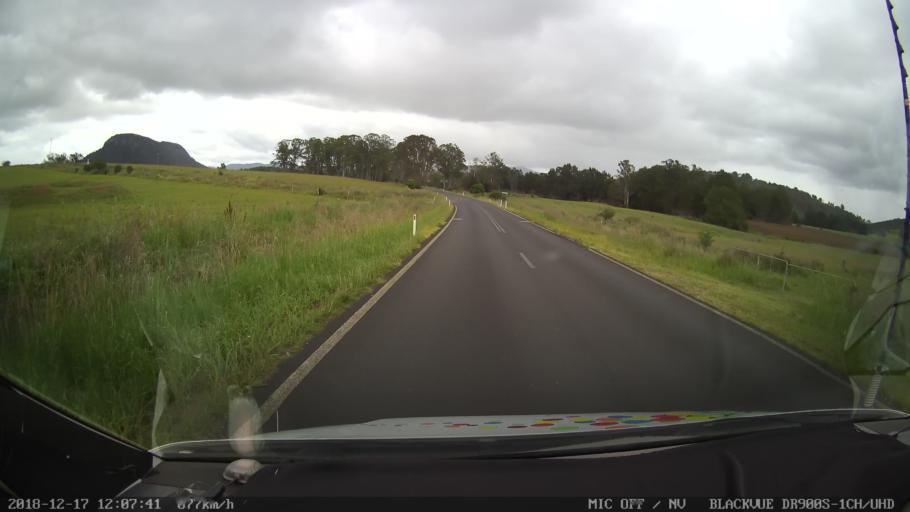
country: AU
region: New South Wales
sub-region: Kyogle
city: Kyogle
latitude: -28.4725
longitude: 152.5629
